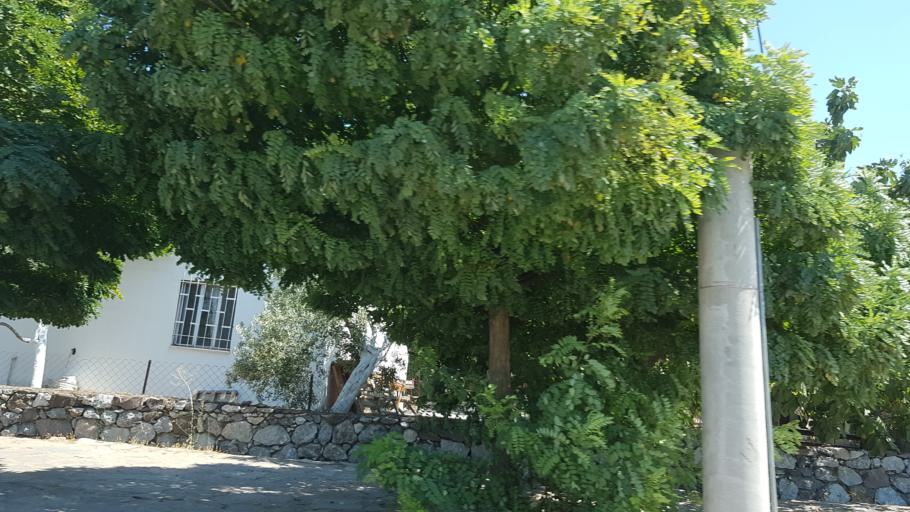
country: TR
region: Mugla
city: Karaova
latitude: 37.1130
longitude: 27.6556
